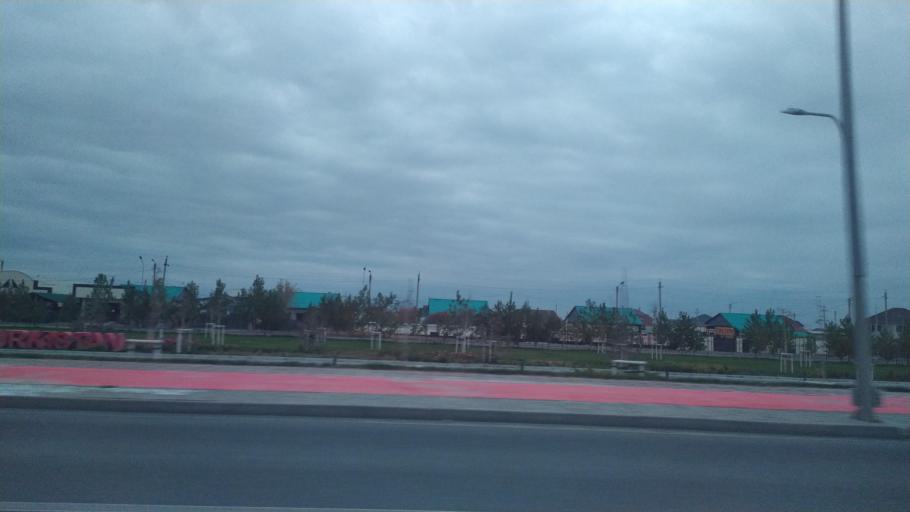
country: KZ
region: Ongtustik Qazaqstan
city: Turkestan
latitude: 43.2775
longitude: 68.3292
